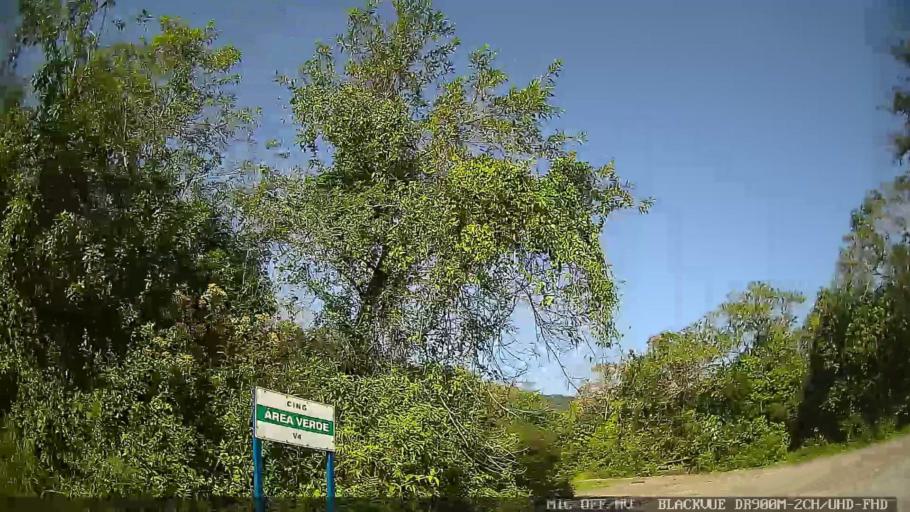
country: BR
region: Sao Paulo
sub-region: Guaruja
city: Guaruja
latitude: -24.0058
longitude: -46.2983
